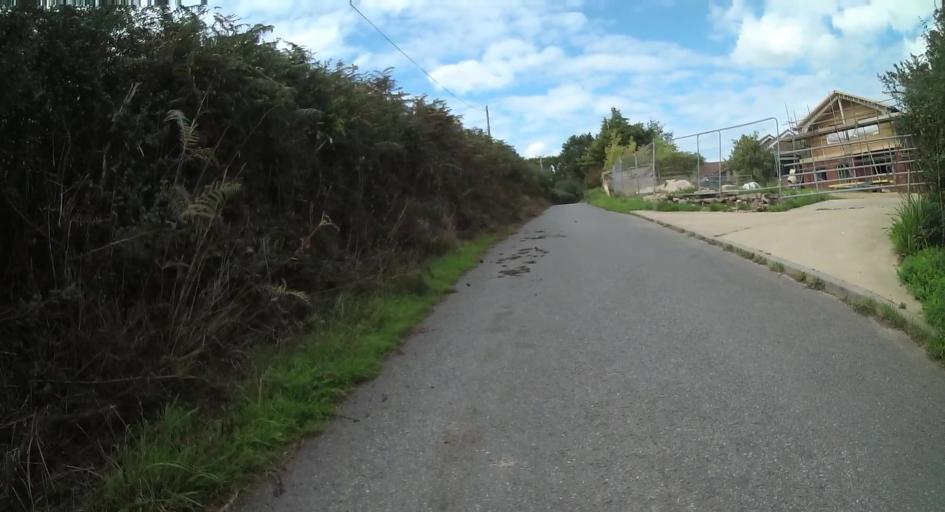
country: GB
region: England
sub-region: Isle of Wight
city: Niton
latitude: 50.6392
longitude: -1.2742
